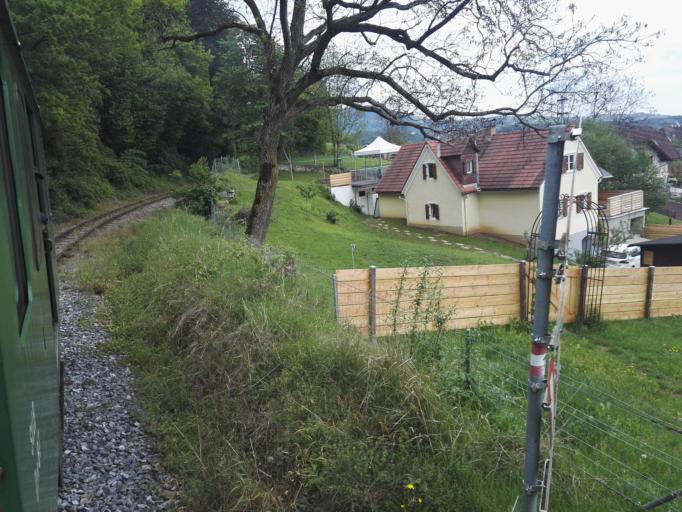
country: AT
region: Styria
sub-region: Politischer Bezirk Weiz
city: Puch bei Weiz
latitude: 47.2303
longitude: 15.6743
